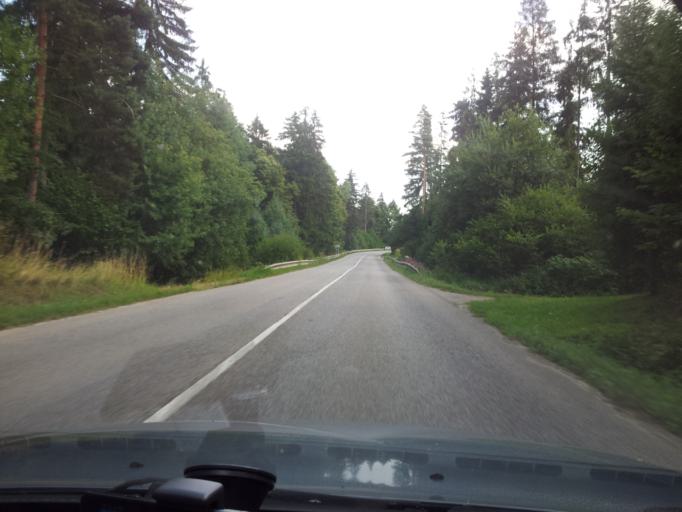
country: SK
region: Zilinsky
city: Namestovo
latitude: 49.4022
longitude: 19.5057
